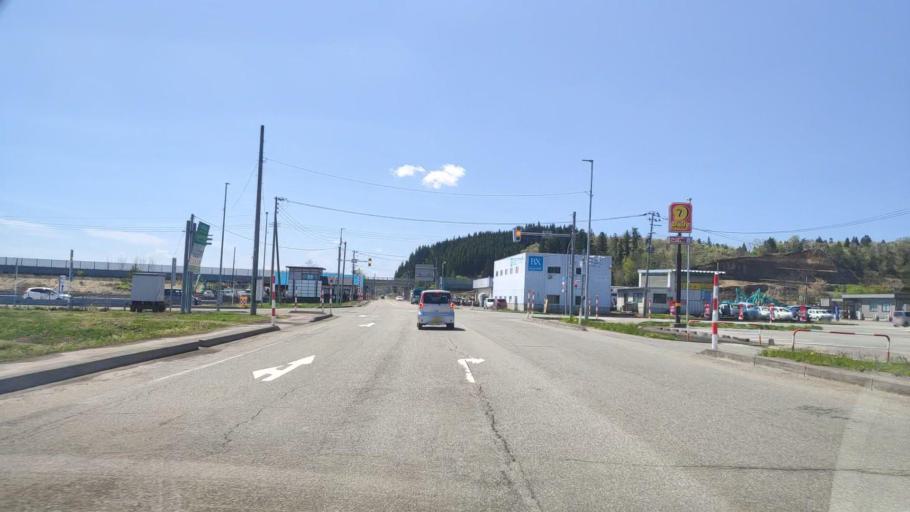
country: JP
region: Akita
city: Omagari
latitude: 39.4328
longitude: 140.4455
